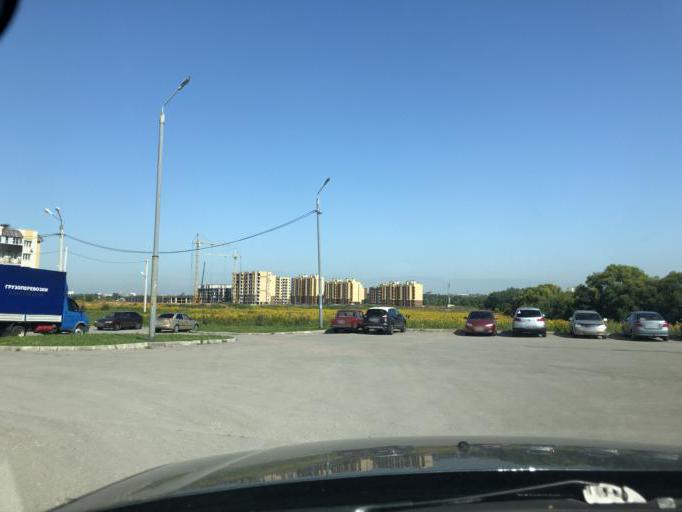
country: RU
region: Tula
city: Tula
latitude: 54.1757
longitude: 37.6574
